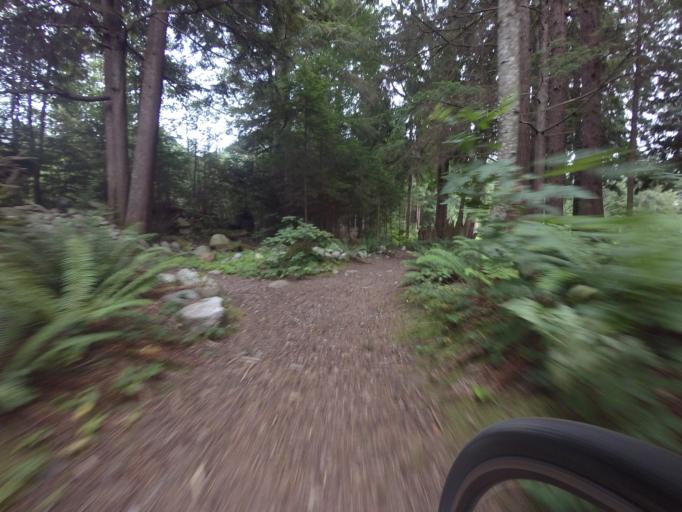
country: CA
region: British Columbia
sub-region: Greater Vancouver Regional District
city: Lions Bay
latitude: 49.5823
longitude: -123.2234
